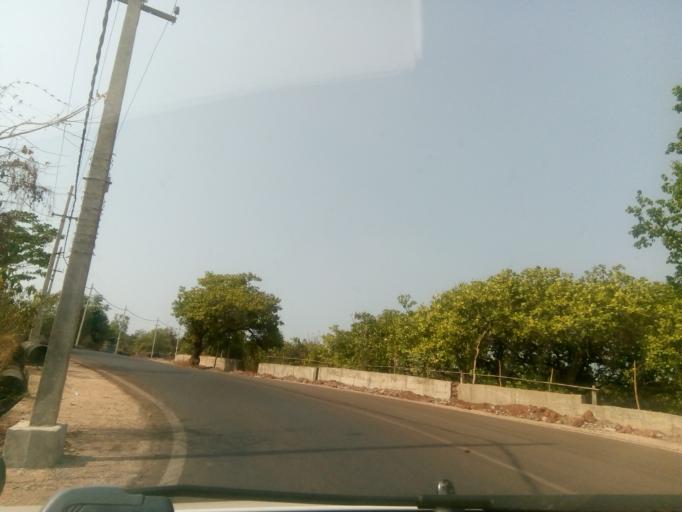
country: IN
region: Goa
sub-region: North Goa
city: Pernem
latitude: 15.7236
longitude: 73.8547
